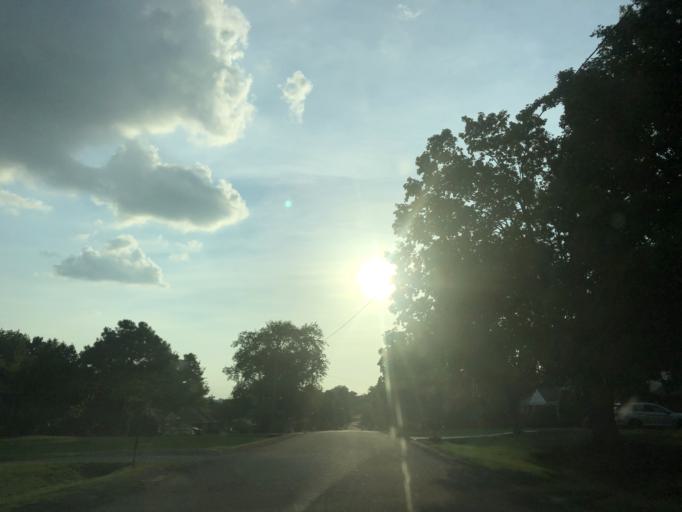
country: US
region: Tennessee
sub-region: Davidson County
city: Nashville
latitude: 36.1671
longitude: -86.7005
